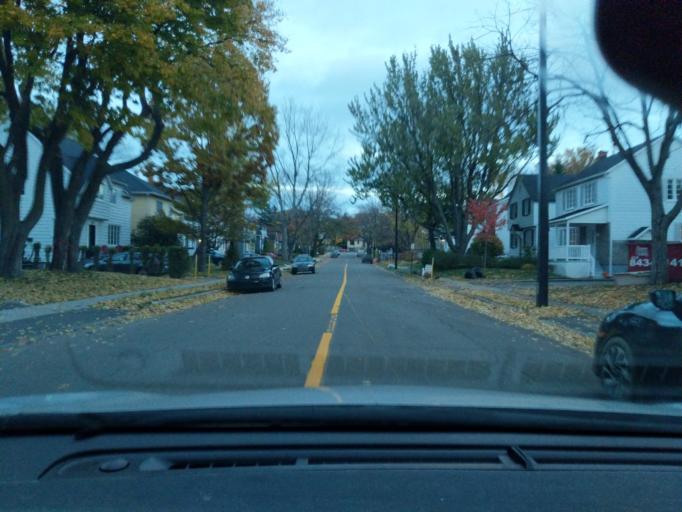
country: CA
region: Quebec
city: Quebec
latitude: 46.7893
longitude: -71.2505
